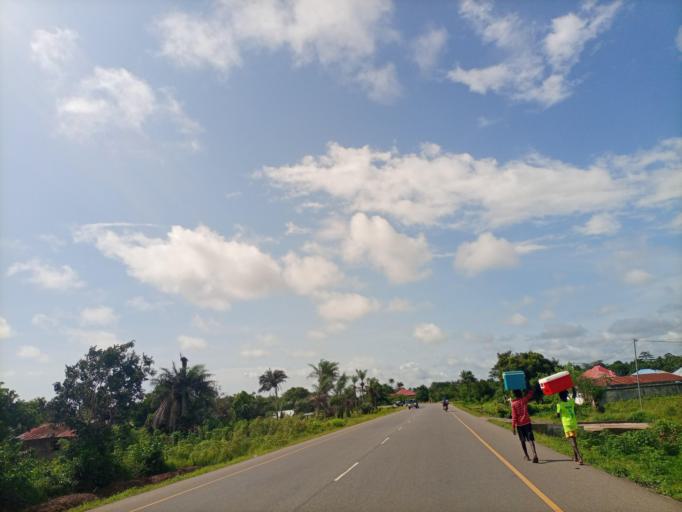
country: SL
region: Northern Province
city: Masoyila
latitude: 8.6142
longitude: -13.1751
